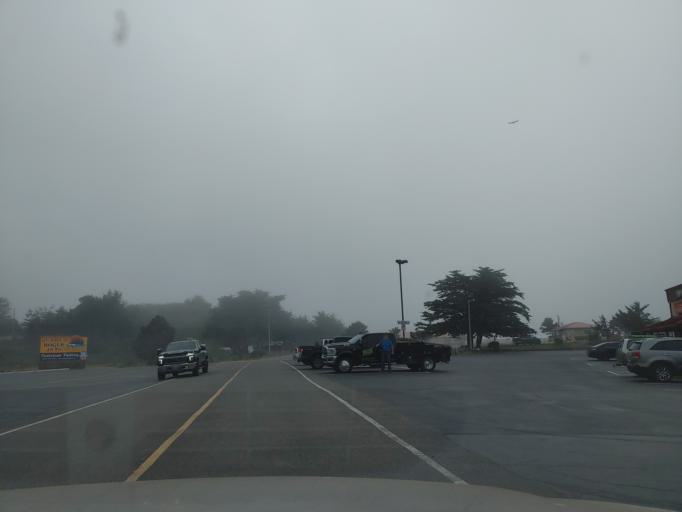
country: US
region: Oregon
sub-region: Curry County
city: Gold Beach
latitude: 42.4213
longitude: -124.4184
